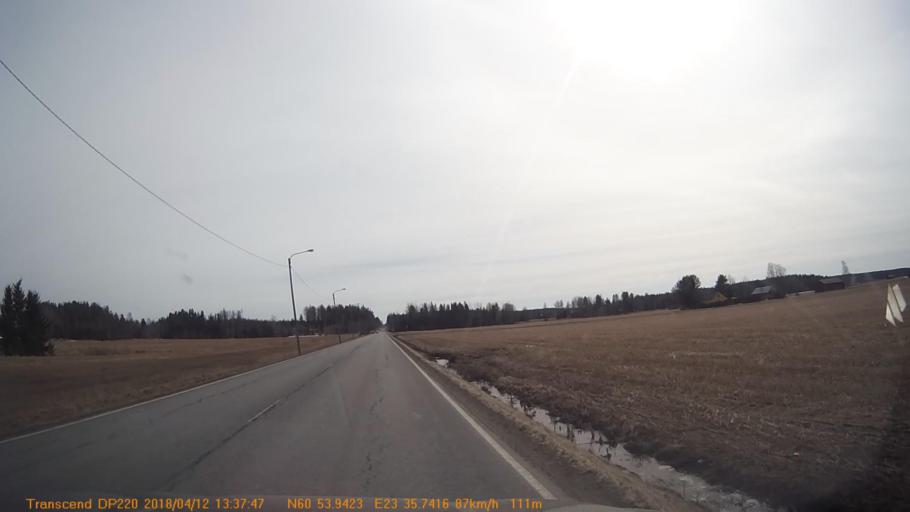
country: FI
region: Haeme
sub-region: Forssa
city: Forssa
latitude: 60.8988
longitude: 23.5958
